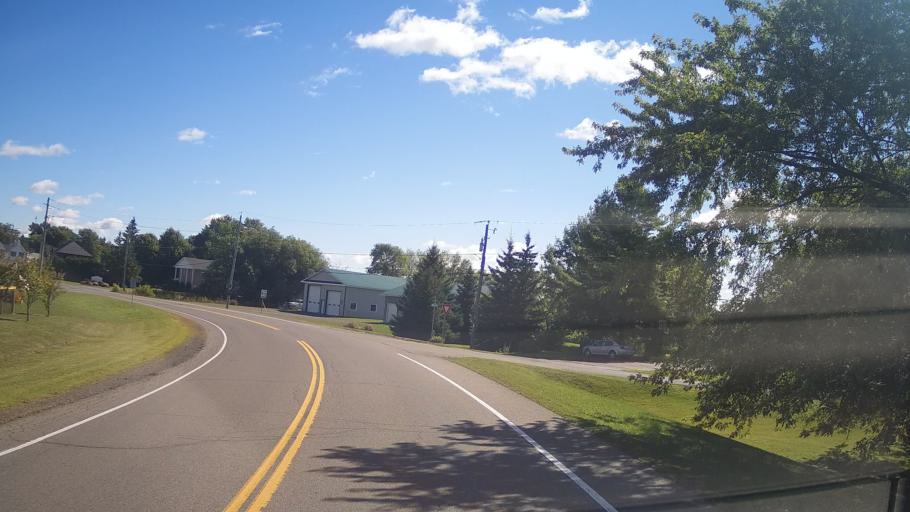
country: US
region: New York
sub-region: St. Lawrence County
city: Norfolk
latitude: 44.9711
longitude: -75.2510
